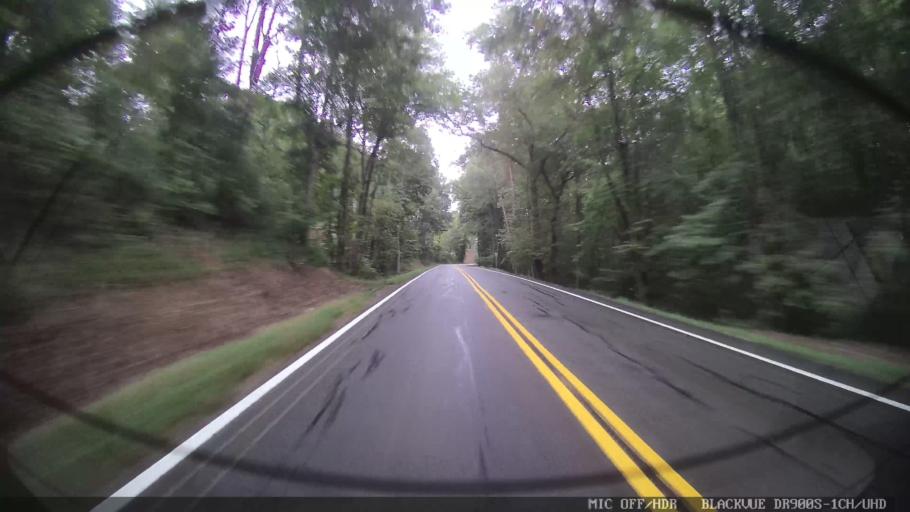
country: US
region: Georgia
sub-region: Gilmer County
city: Ellijay
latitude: 34.7393
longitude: -84.5201
